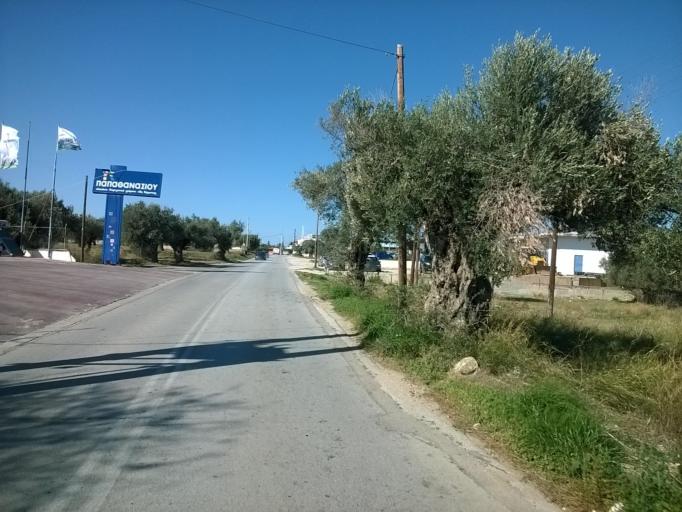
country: GR
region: Attica
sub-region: Nomarchia Anatolikis Attikis
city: Keratea
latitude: 37.8027
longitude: 23.9923
